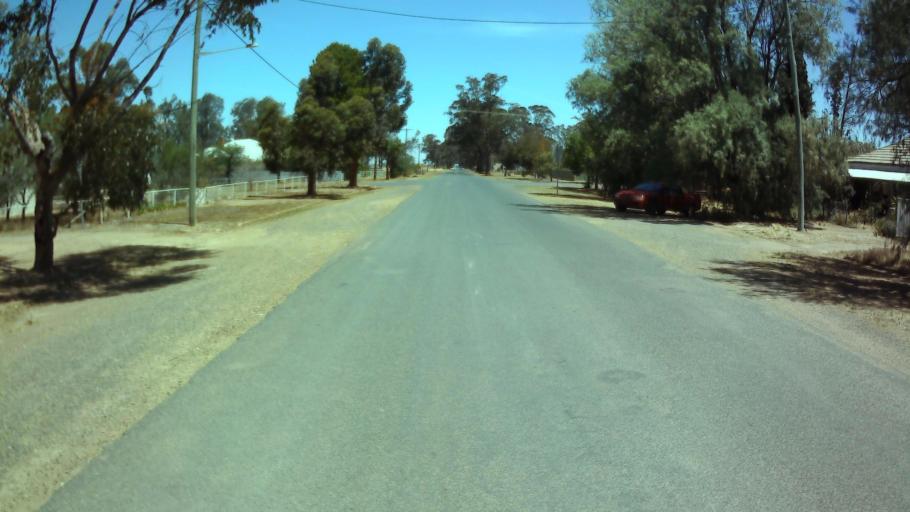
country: AU
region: New South Wales
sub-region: Weddin
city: Grenfell
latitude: -34.0126
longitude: 147.7943
